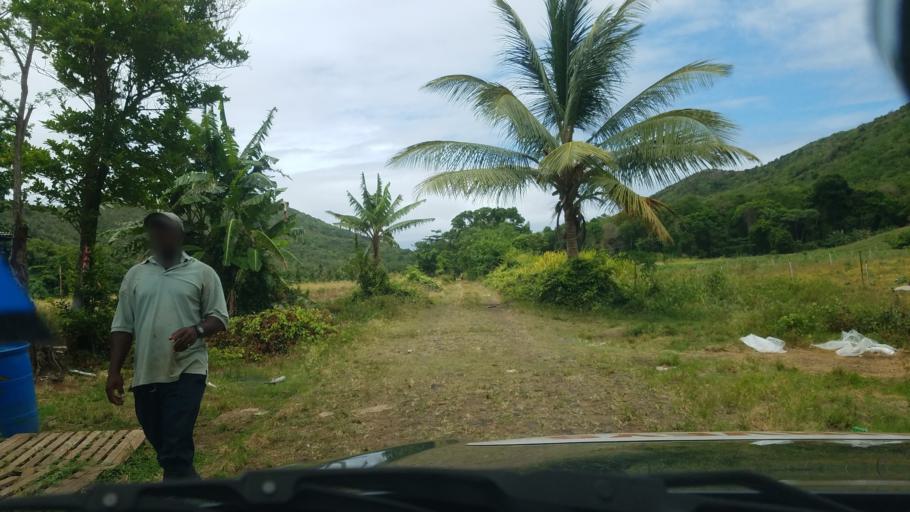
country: LC
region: Gros-Islet
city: Gros Islet
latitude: 14.0283
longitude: -60.9065
